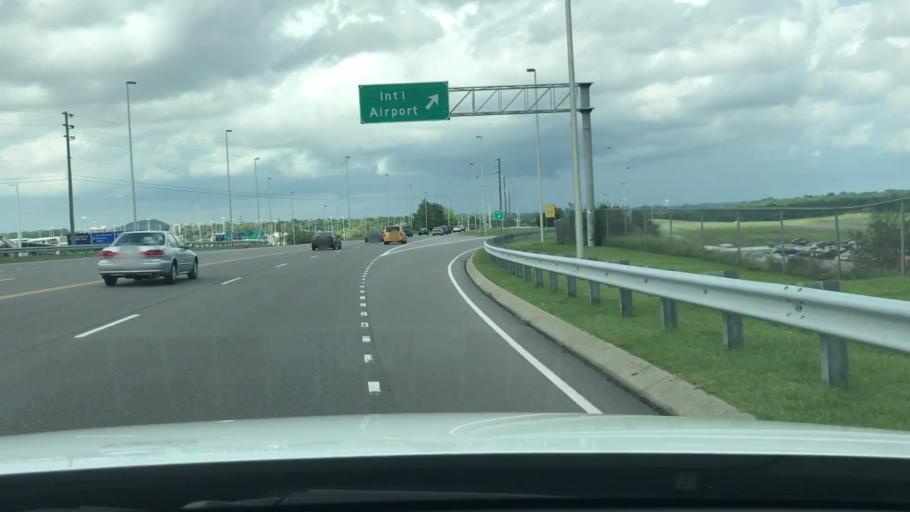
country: US
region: Tennessee
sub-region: Davidson County
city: Lakewood
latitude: 36.1289
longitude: -86.6653
